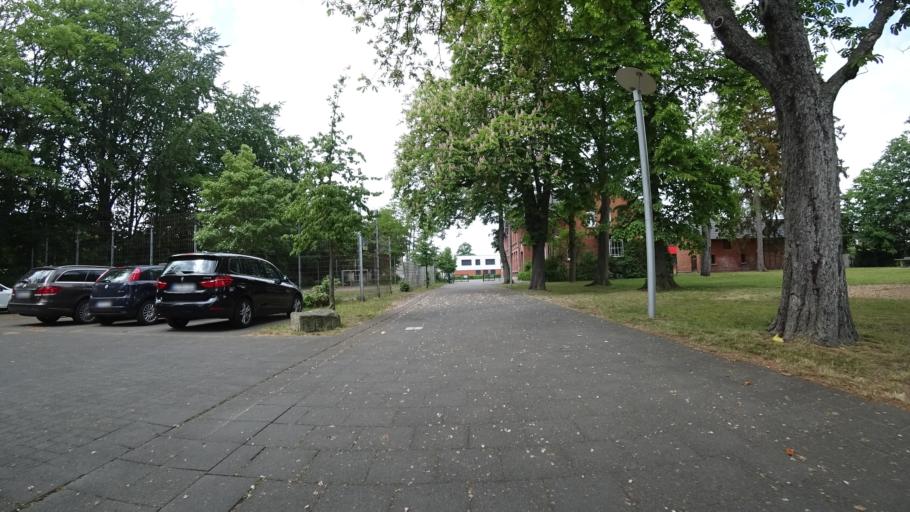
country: DE
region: North Rhine-Westphalia
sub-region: Regierungsbezirk Detmold
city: Guetersloh
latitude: 51.9067
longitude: 8.3951
